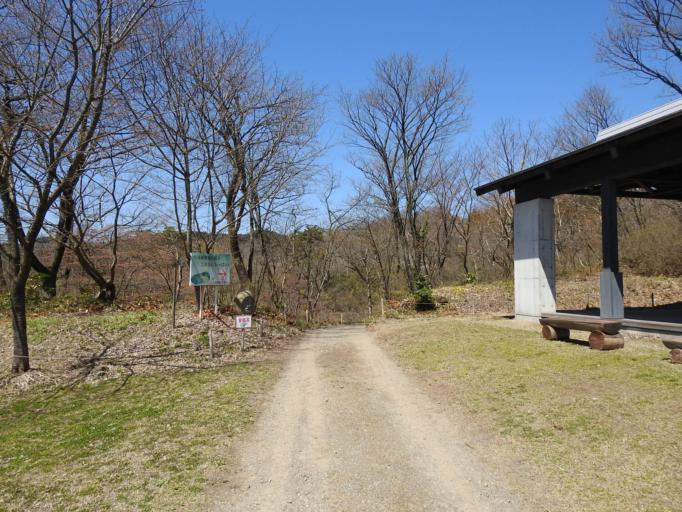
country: JP
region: Niigata
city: Nagaoka
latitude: 37.4622
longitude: 138.7457
